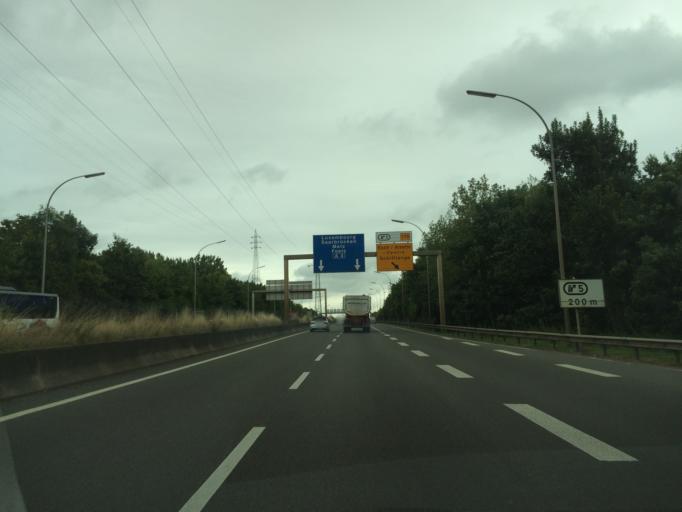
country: LU
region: Luxembourg
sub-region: Canton d'Esch-sur-Alzette
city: Esch-sur-Alzette
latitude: 49.5133
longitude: 5.9812
